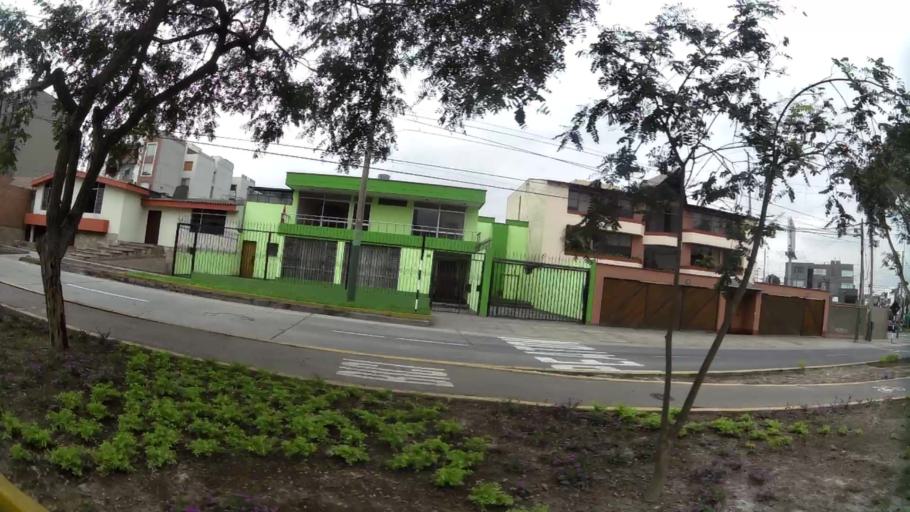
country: PE
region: Lima
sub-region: Lima
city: San Luis
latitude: -12.1096
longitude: -76.9803
